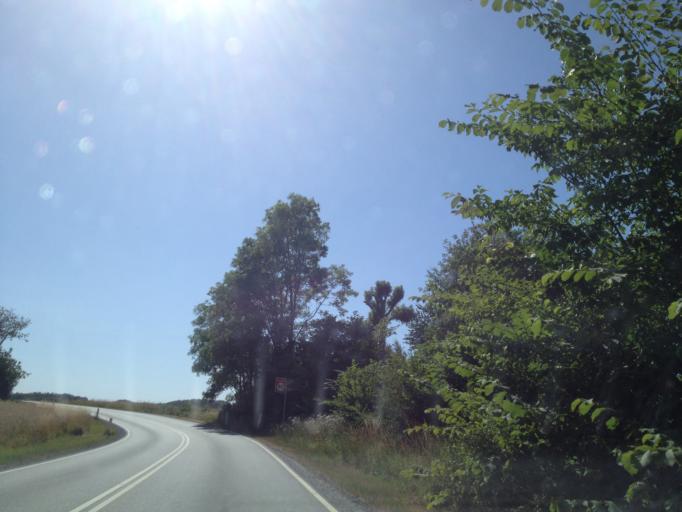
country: DK
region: Capital Region
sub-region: Helsingor Kommune
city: Hornbaek
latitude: 56.0422
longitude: 12.4125
